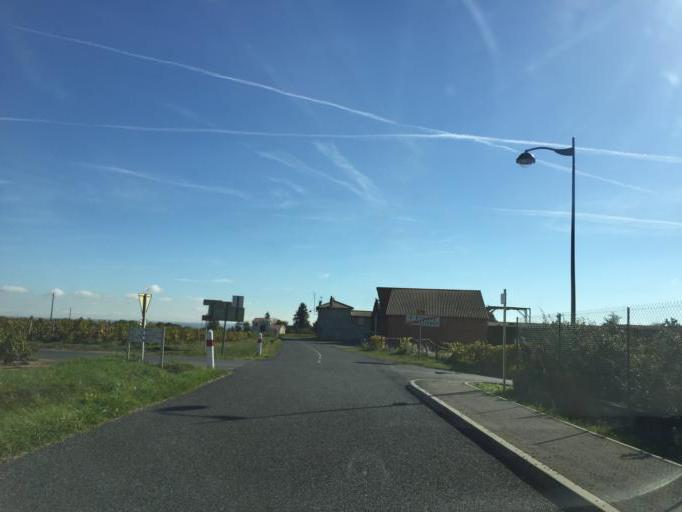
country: FR
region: Rhone-Alpes
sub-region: Departement du Rhone
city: Charentay
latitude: 46.0667
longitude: 4.6531
